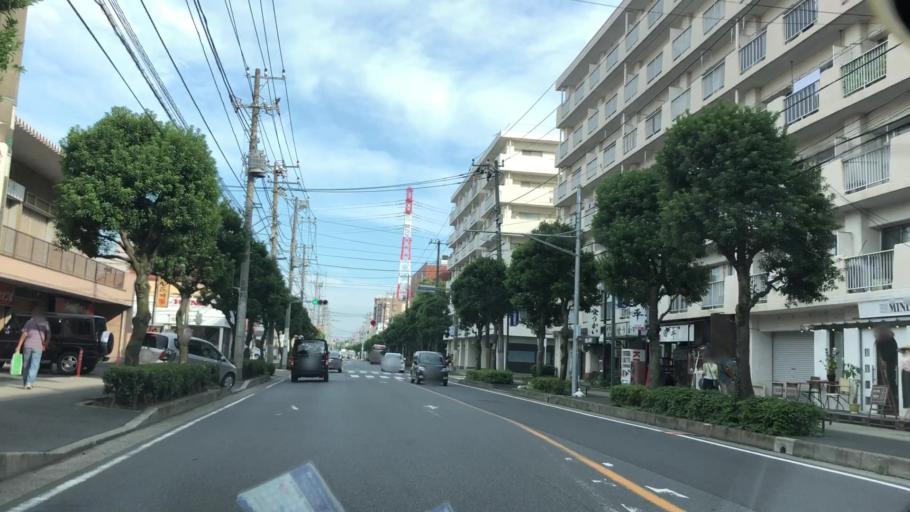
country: JP
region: Tokyo
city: Urayasu
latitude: 35.6803
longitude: 139.9175
